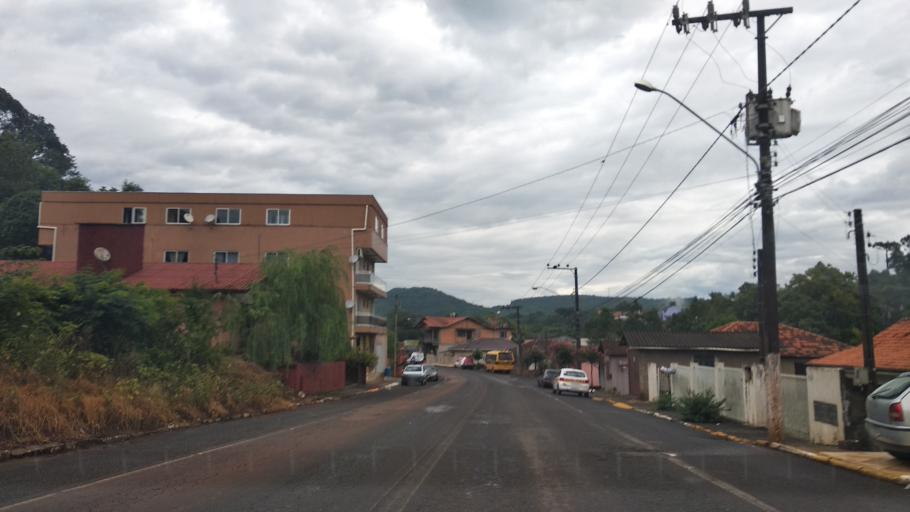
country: BR
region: Santa Catarina
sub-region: Videira
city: Videira
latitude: -27.0990
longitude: -51.2496
